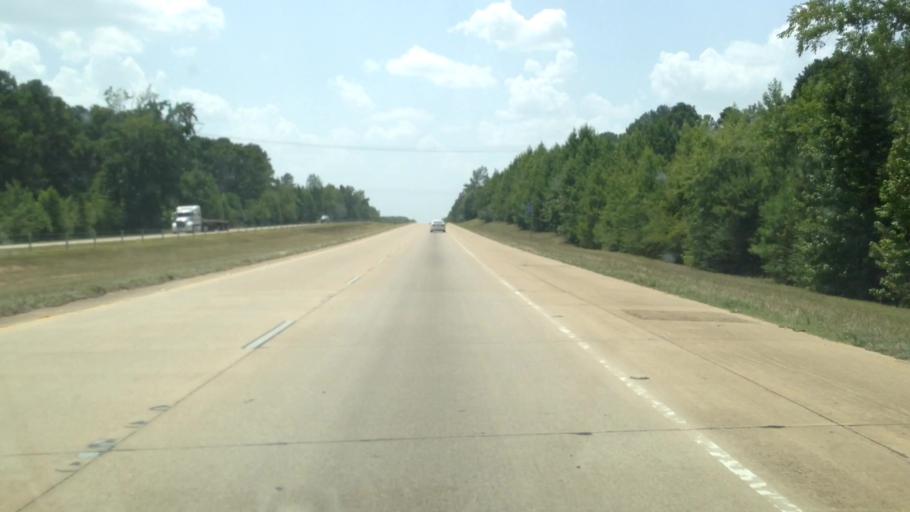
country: US
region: Louisiana
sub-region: Lincoln Parish
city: Grambling
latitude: 32.5424
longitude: -92.7204
